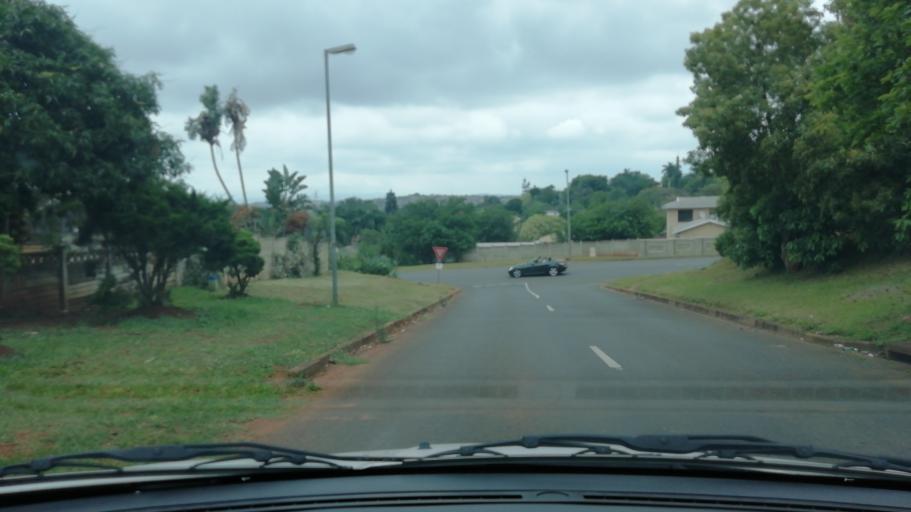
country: ZA
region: KwaZulu-Natal
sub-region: uThungulu District Municipality
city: Empangeni
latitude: -28.7694
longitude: 31.8955
